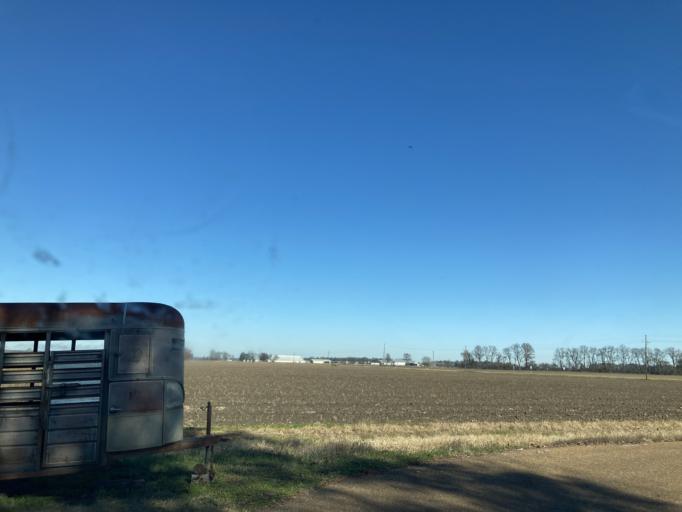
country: US
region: Mississippi
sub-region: Sharkey County
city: Rolling Fork
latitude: 32.8260
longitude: -90.7087
